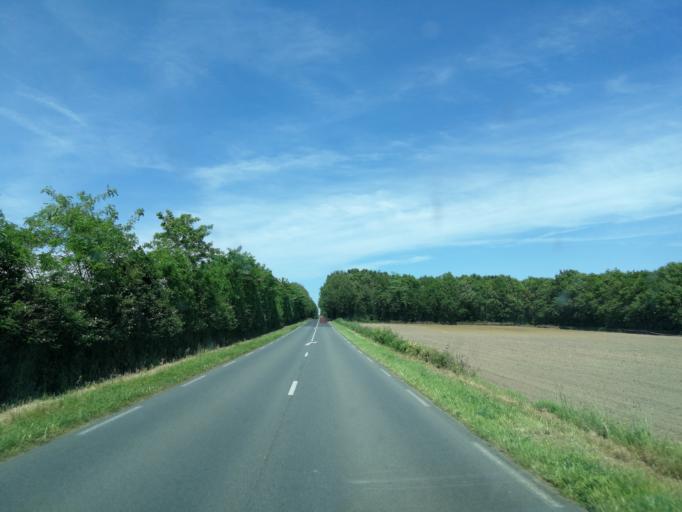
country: FR
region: Poitou-Charentes
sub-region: Departement des Deux-Sevres
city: Saint-Varent
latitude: 46.9308
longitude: -0.2516
